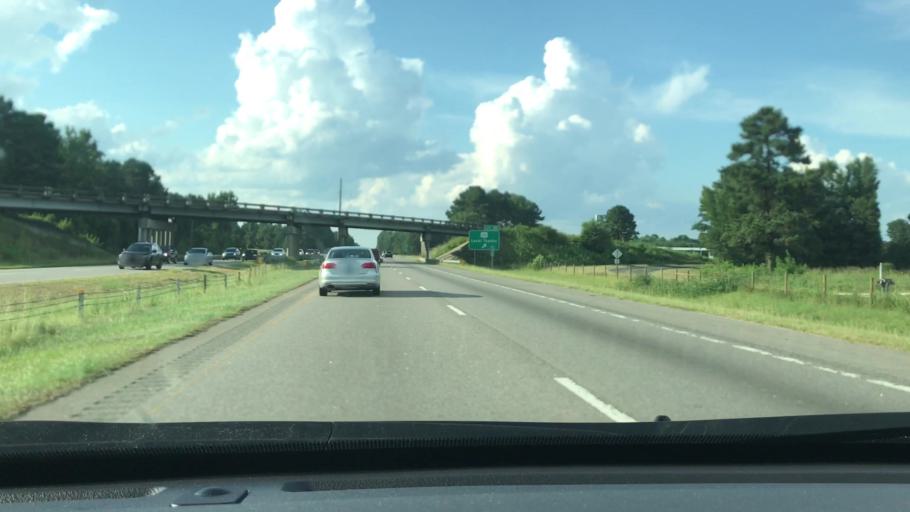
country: US
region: North Carolina
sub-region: Robeson County
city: Saint Pauls
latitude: 34.7192
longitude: -78.9973
